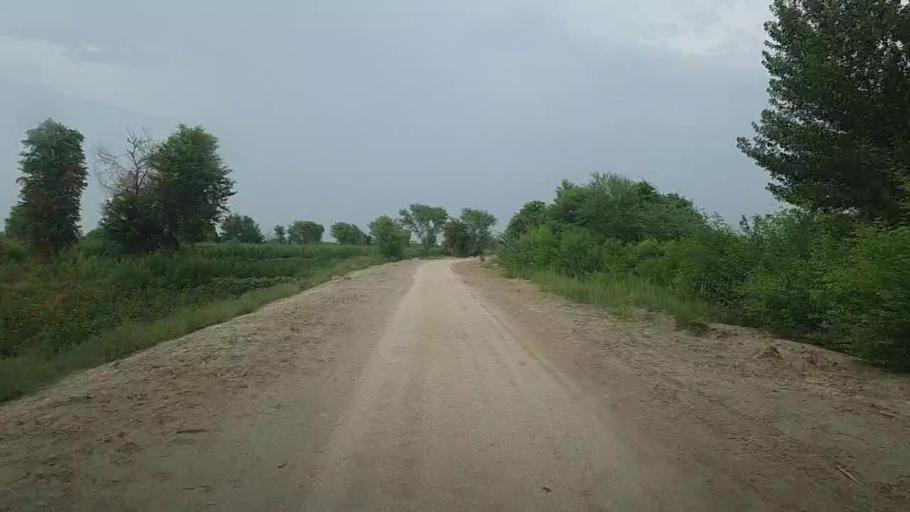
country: PK
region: Sindh
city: Karaundi
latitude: 26.9720
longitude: 68.4270
